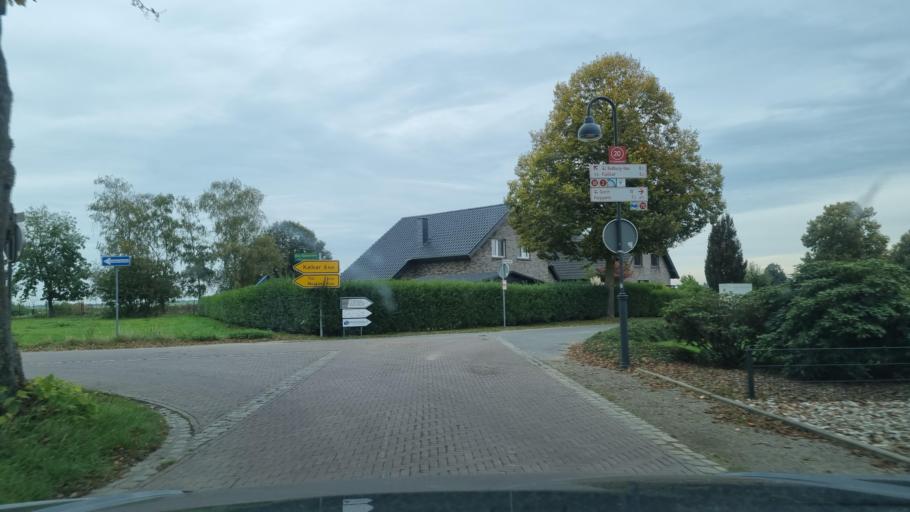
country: DE
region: North Rhine-Westphalia
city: Kalkar
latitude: 51.7268
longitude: 6.2331
